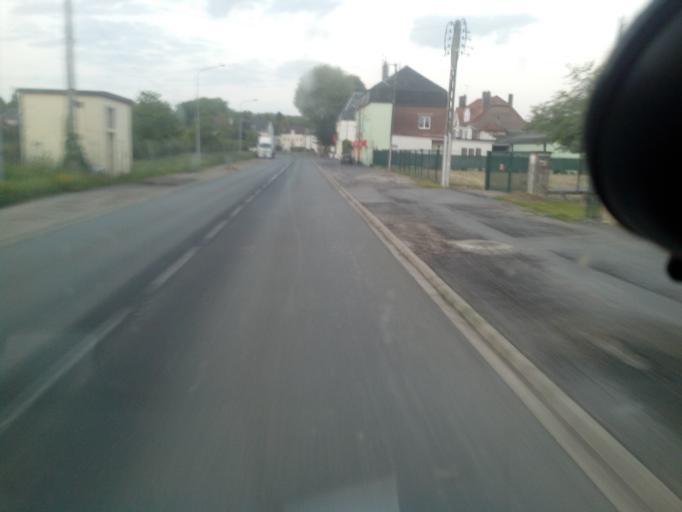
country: FR
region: Nord-Pas-de-Calais
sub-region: Departement du Pas-de-Calais
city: Hesdin
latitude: 50.3774
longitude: 2.0329
